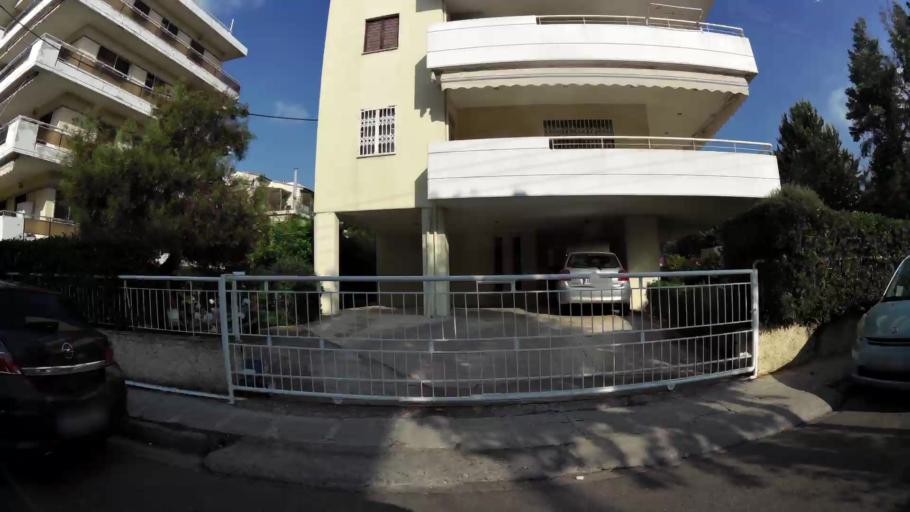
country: GR
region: Attica
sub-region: Nomarchia Athinas
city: Cholargos
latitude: 38.0071
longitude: 23.8065
